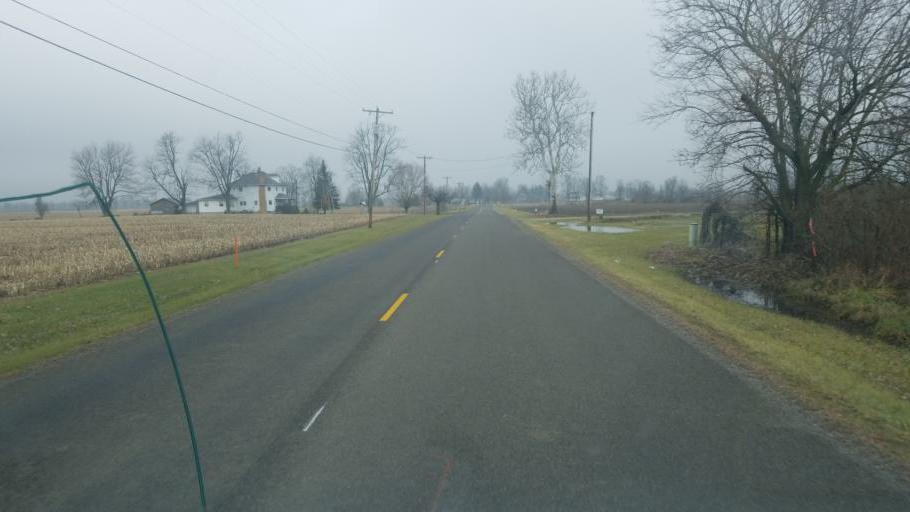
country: US
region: Ohio
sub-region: Champaign County
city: North Lewisburg
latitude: 40.3380
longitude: -83.5681
